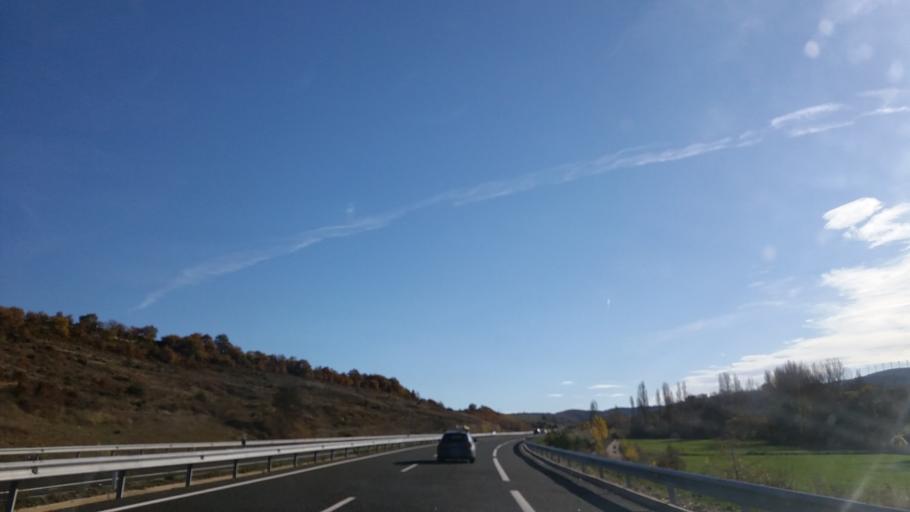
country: ES
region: Navarre
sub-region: Provincia de Navarra
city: Monreal
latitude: 42.6806
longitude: -1.4652
